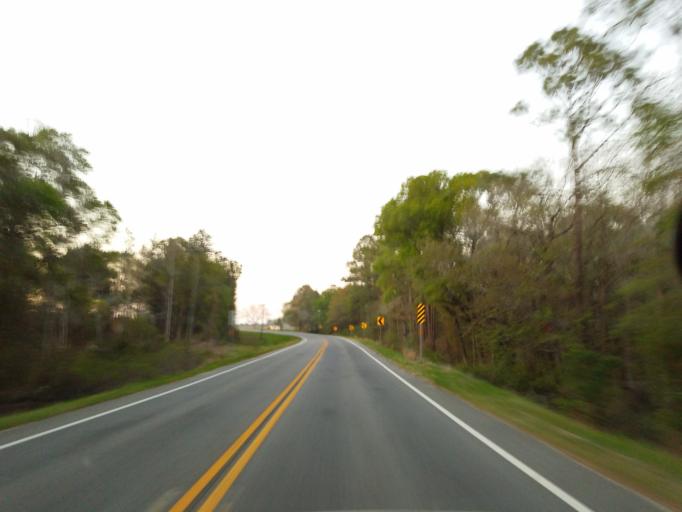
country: US
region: Georgia
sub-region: Berrien County
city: Nashville
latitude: 31.2625
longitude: -83.3202
